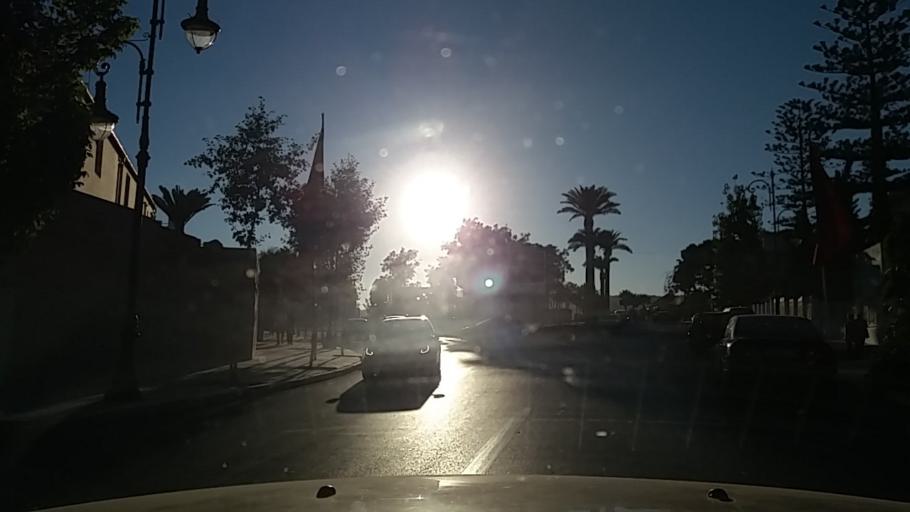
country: MA
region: Tanger-Tetouan
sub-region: Tanger-Assilah
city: Tangier
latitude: 35.7801
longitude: -5.8264
